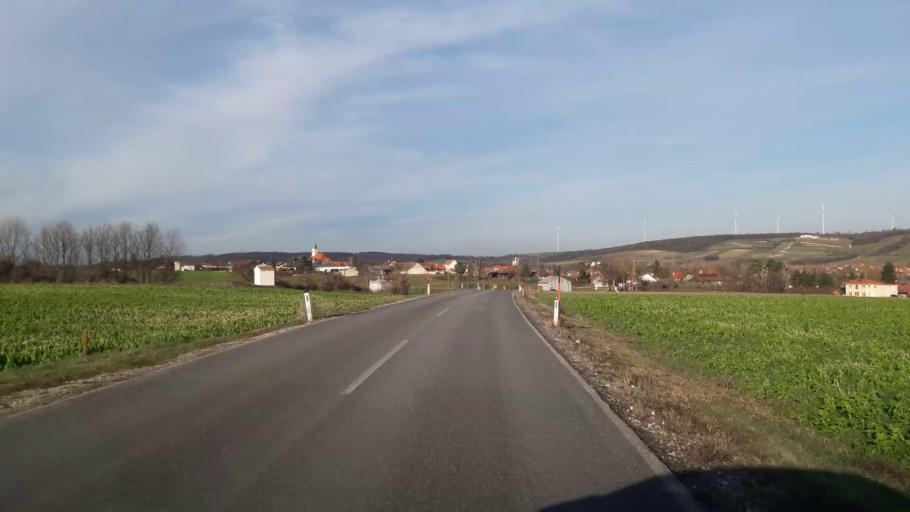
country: AT
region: Lower Austria
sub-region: Politischer Bezirk Ganserndorf
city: Gross-Schweinbarth
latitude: 48.4061
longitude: 16.6338
